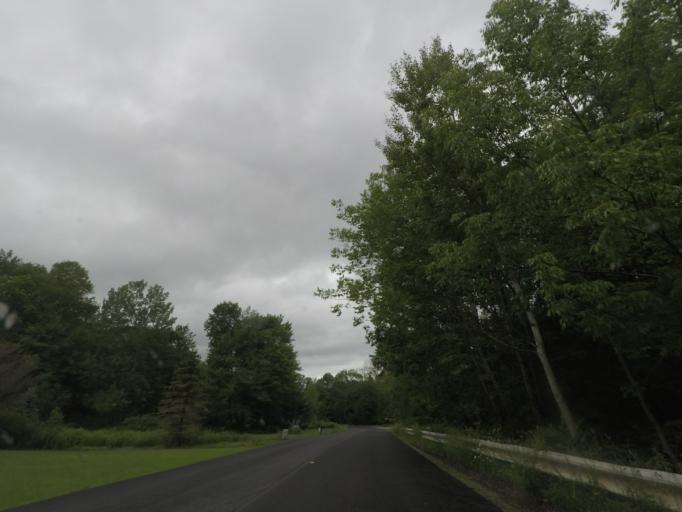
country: US
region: New York
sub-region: Rensselaer County
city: Poestenkill
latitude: 42.6896
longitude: -73.4787
